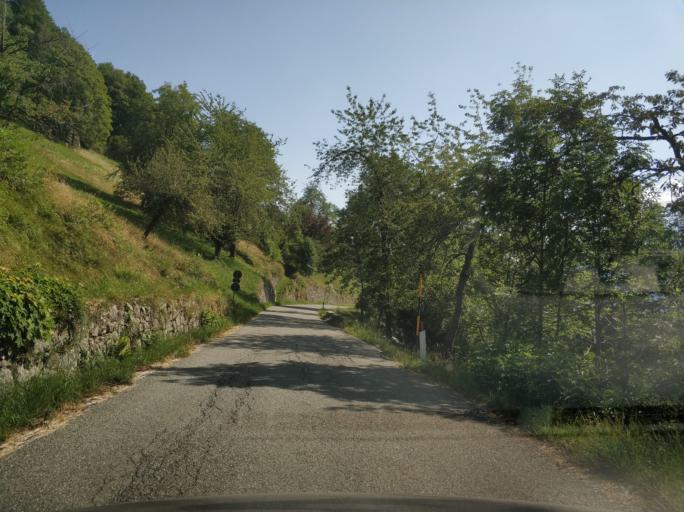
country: IT
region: Piedmont
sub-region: Provincia di Torino
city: Viu
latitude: 45.1913
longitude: 7.3669
